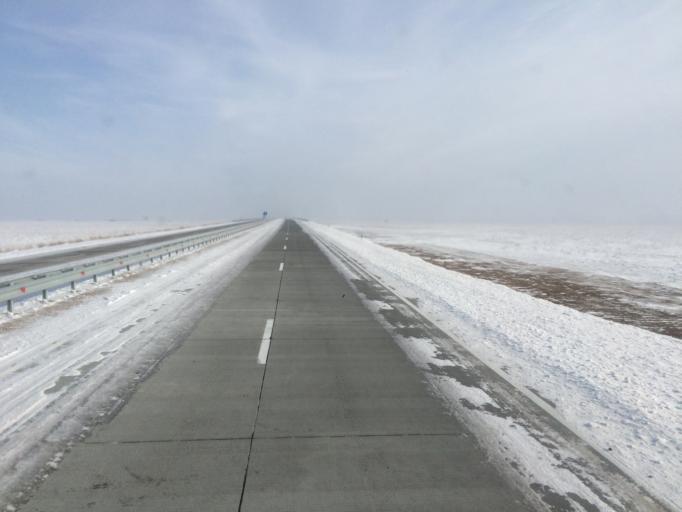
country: KZ
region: Zhambyl
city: Georgiyevka
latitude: 43.3425
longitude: 74.3987
